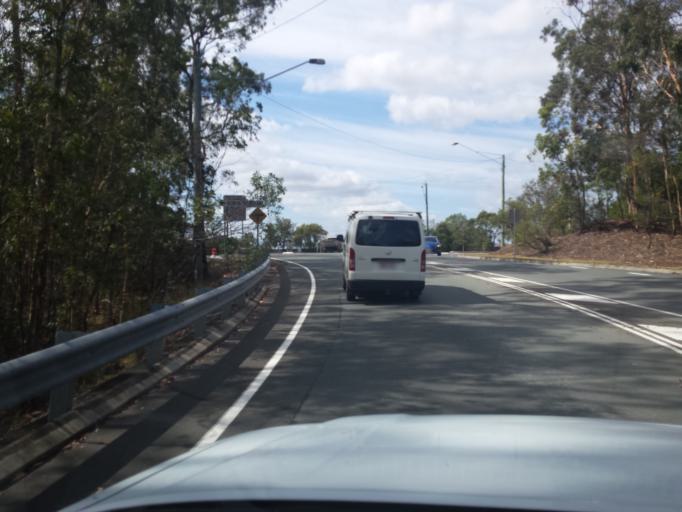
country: AU
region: Queensland
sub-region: Moreton Bay
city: Ferny Hills
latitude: -27.3807
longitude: 152.9482
